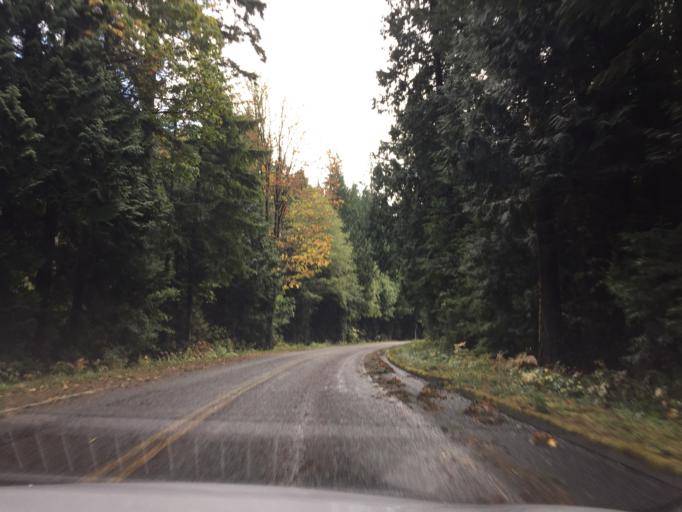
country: US
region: Washington
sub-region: Whatcom County
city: Sudden Valley
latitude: 48.7328
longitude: -122.3114
